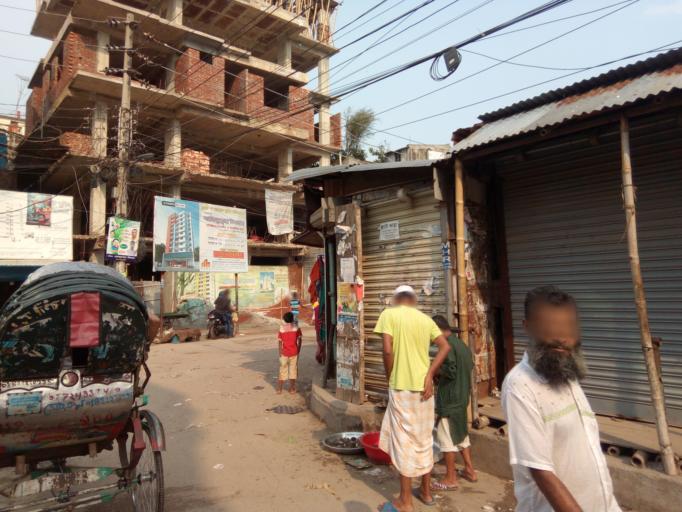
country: BD
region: Dhaka
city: Paltan
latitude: 23.7230
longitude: 90.4321
